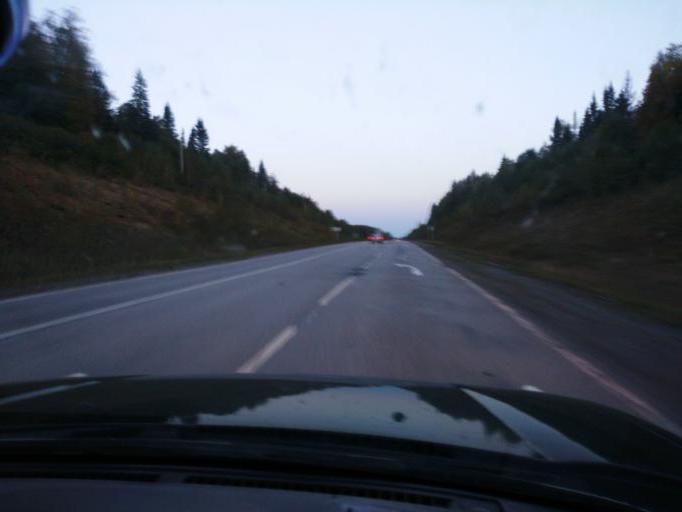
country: RU
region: Perm
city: Verkhnechusovskiye Gorodki
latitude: 58.2767
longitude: 56.9342
